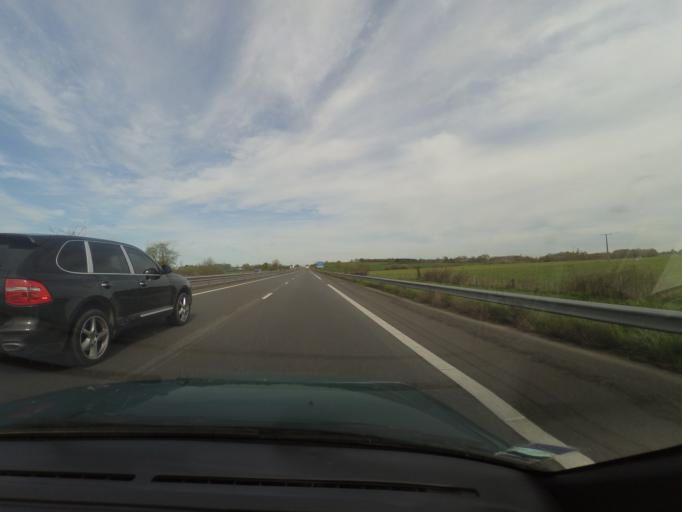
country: FR
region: Pays de la Loire
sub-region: Departement de la Loire-Atlantique
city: Le Bignon
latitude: 47.0829
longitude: -1.4489
